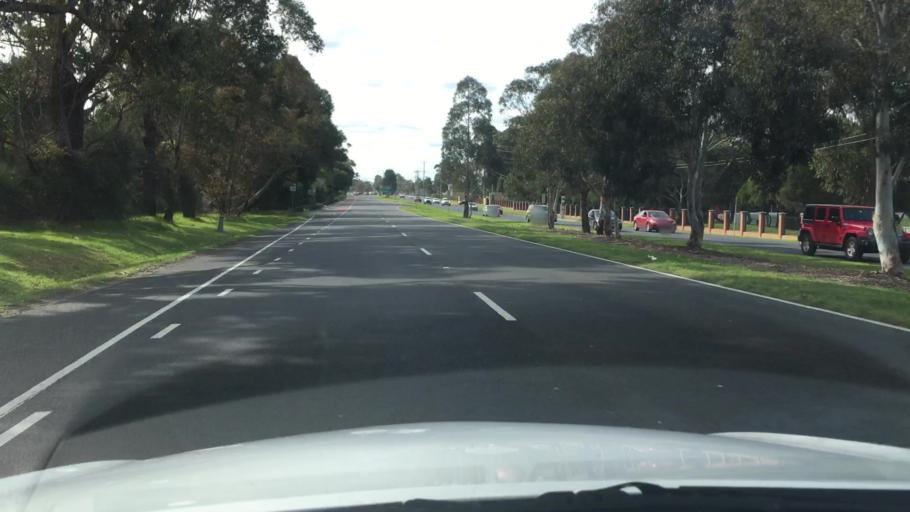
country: AU
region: Victoria
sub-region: Kingston
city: Dingley Village
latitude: -37.9962
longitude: 145.1435
